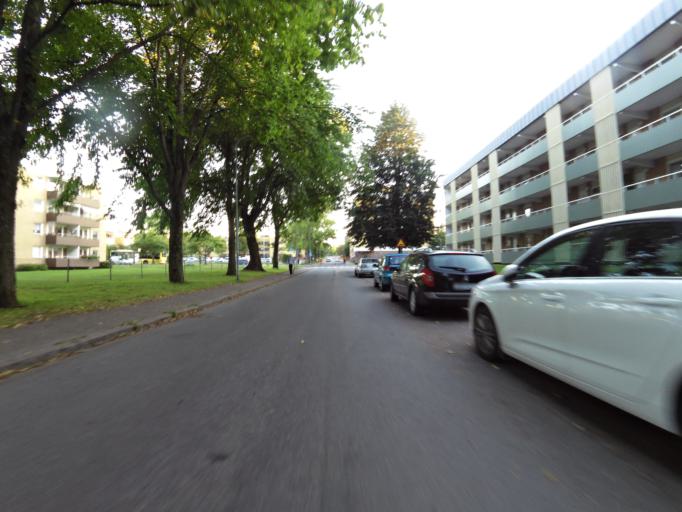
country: SE
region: Gaevleborg
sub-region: Gavle Kommun
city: Gavle
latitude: 60.6743
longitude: 17.1653
